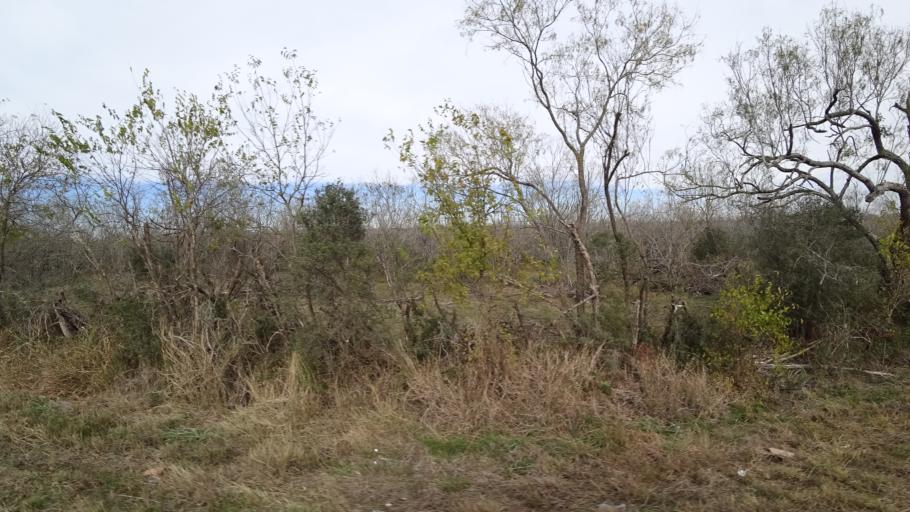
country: US
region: Texas
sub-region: Travis County
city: Garfield
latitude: 30.1401
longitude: -97.6122
